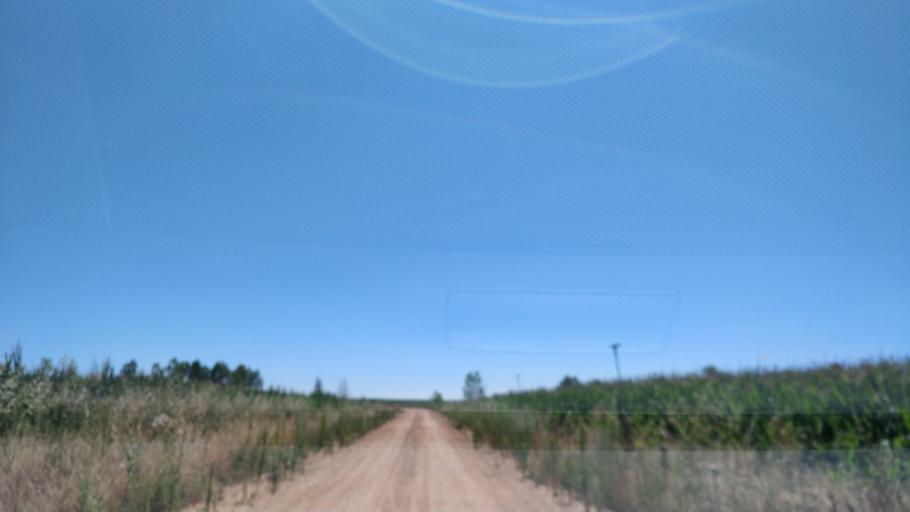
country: ES
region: Castille and Leon
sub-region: Provincia de Leon
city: Bustillo del Paramo
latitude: 42.4745
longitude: -5.8073
